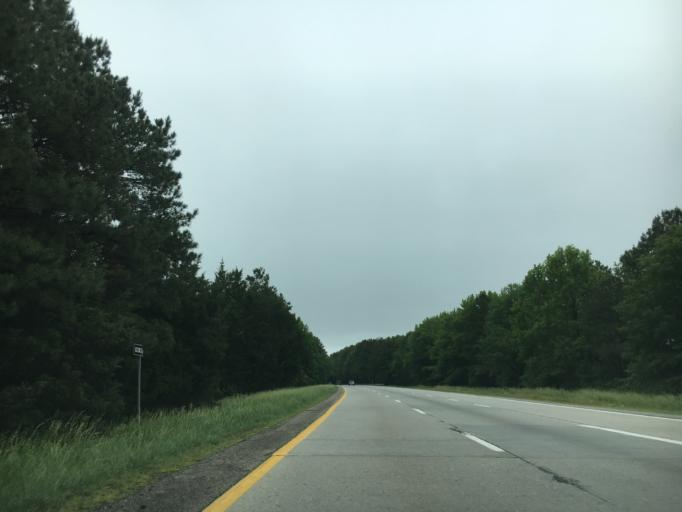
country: US
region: Virginia
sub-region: Chesterfield County
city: Matoaca
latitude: 37.1839
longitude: -77.4923
